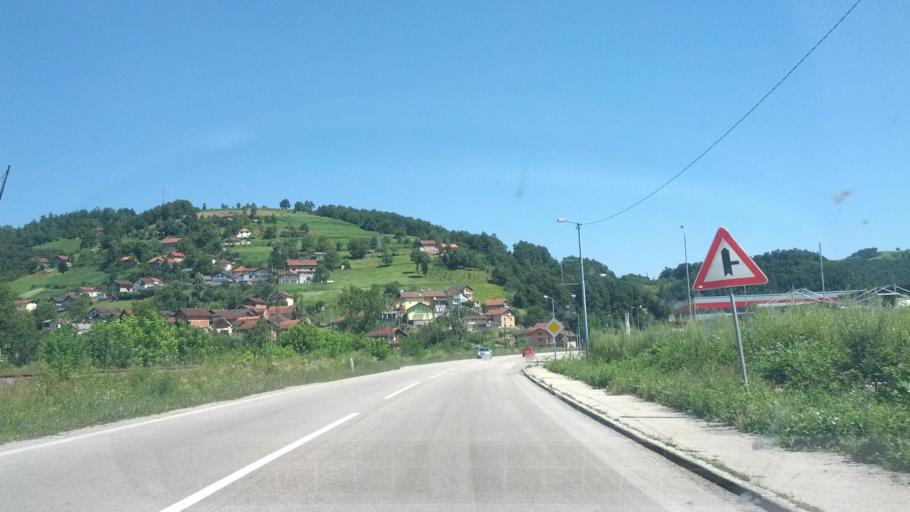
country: BA
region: Federation of Bosnia and Herzegovina
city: Bosanska Krupa
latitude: 44.8937
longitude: 16.1541
